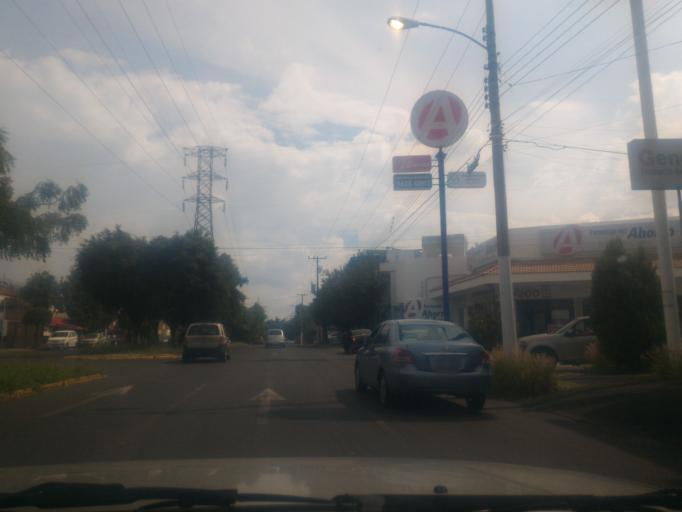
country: MX
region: Jalisco
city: Guadalajara
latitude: 20.6742
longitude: -103.4166
